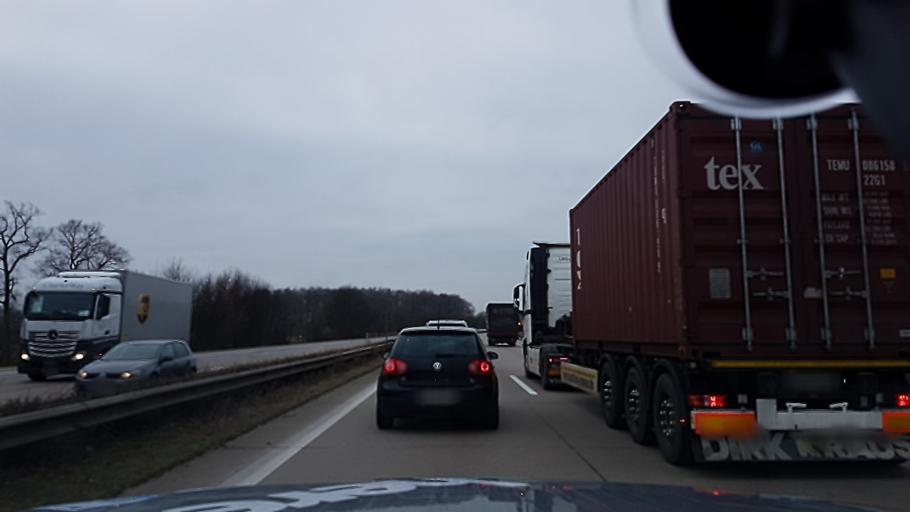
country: DE
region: Schleswig-Holstein
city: Stapelfeld
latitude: 53.6021
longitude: 10.2286
